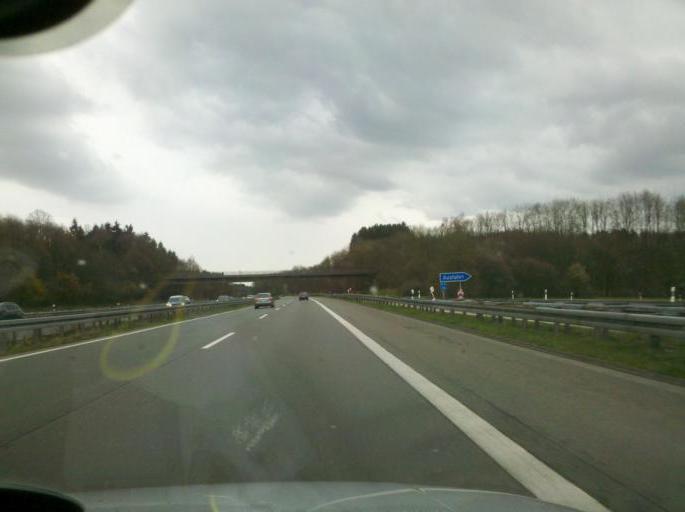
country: DE
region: North Rhine-Westphalia
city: Bergneustadt
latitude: 50.9750
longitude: 7.6441
